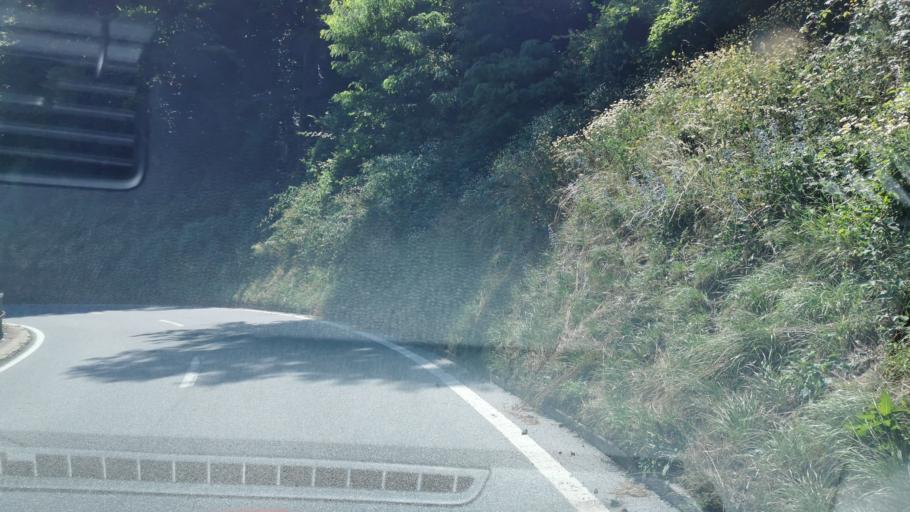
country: IT
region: Lombardy
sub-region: Provincia di Como
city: Campione
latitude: 45.9510
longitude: 8.9810
